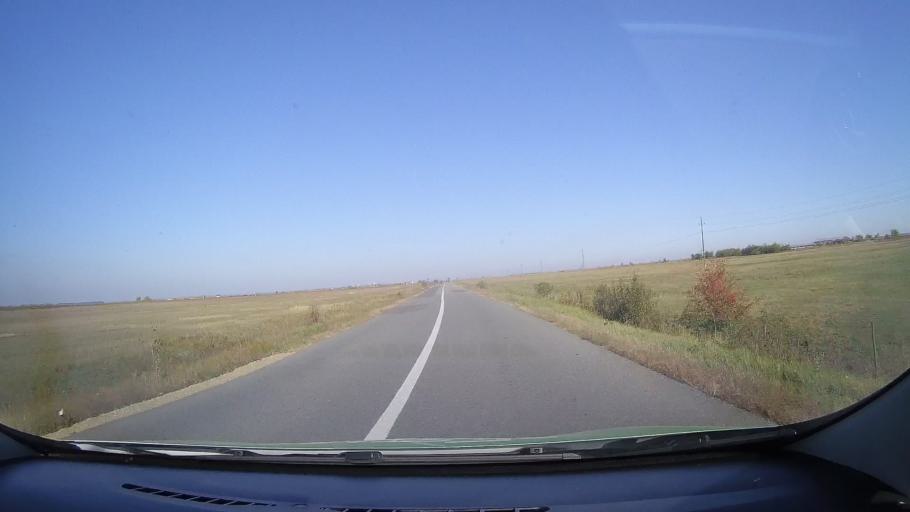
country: RO
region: Satu Mare
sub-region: Comuna Cauas
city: Cauas
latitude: 47.5418
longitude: 22.5641
